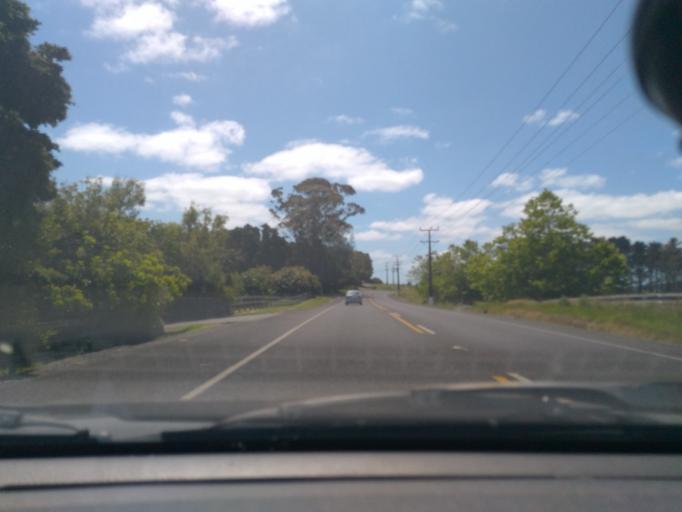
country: NZ
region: Auckland
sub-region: Auckland
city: Pakuranga
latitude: -36.9043
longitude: 175.0075
